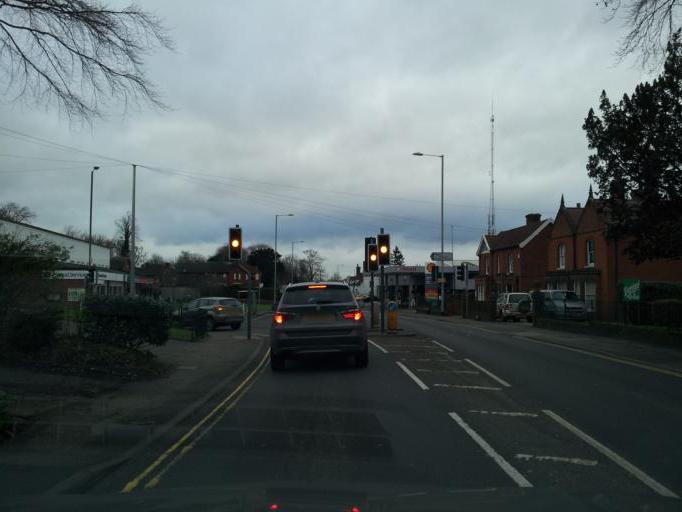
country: GB
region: England
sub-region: Norfolk
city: Long Stratton
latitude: 52.4849
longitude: 1.2336
